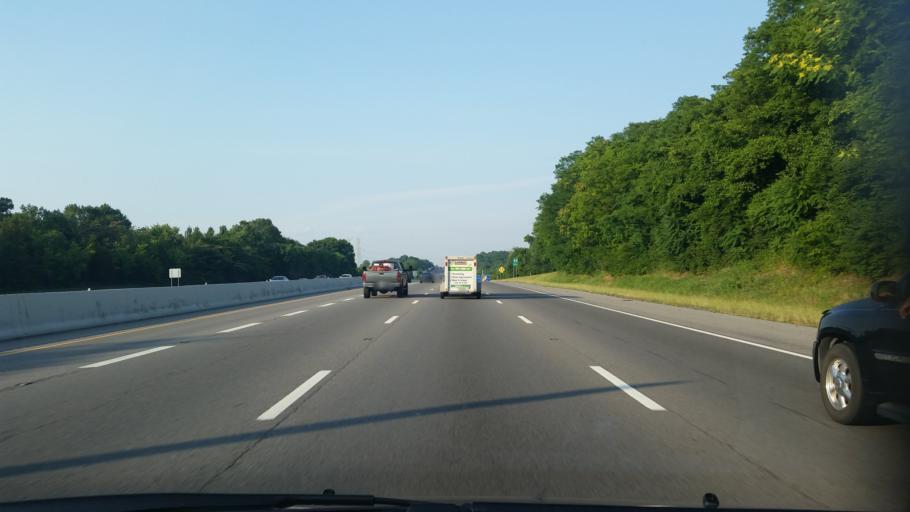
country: US
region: Tennessee
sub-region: Davidson County
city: Lakewood
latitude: 36.1565
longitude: -86.6278
